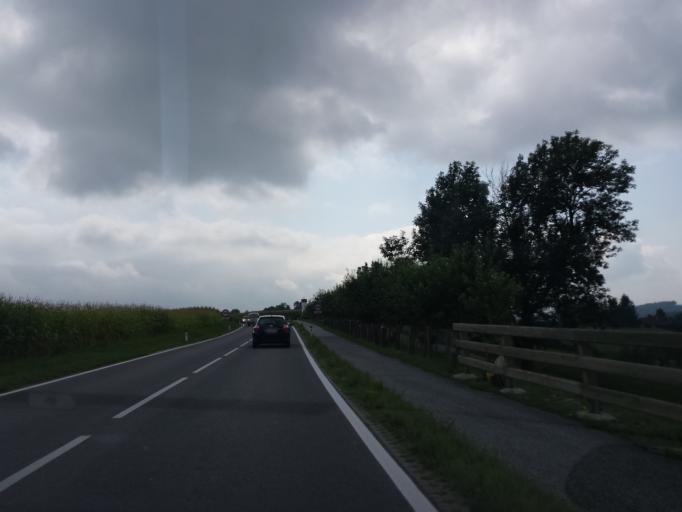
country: AT
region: Styria
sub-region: Politischer Bezirk Deutschlandsberg
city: Rassach
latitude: 46.8640
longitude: 15.2647
